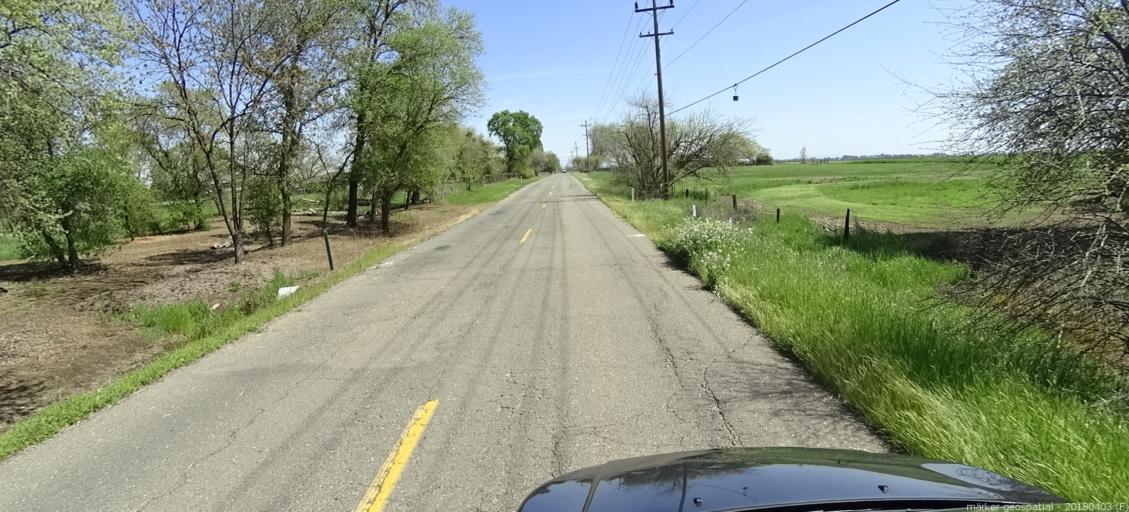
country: US
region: California
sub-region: Sacramento County
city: Wilton
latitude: 38.3798
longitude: -121.2726
